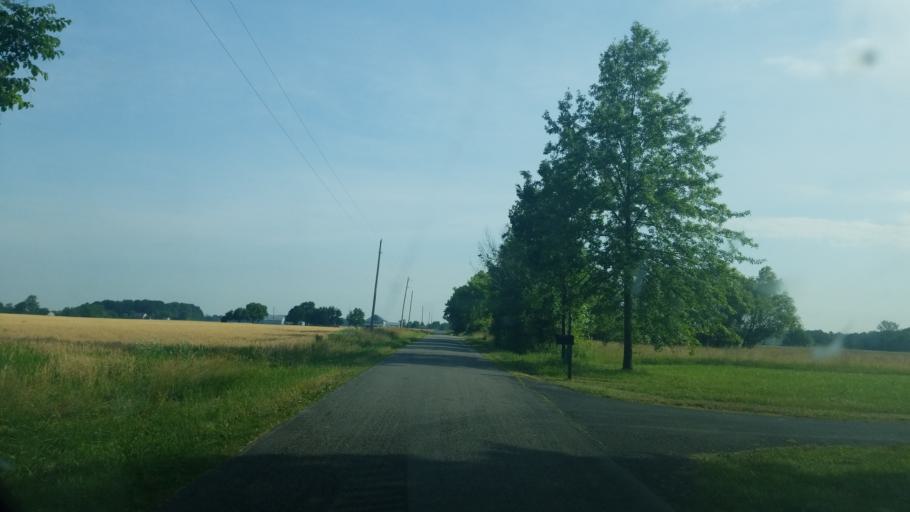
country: US
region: Ohio
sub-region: Hancock County
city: Arlington
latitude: 40.8413
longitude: -83.6704
